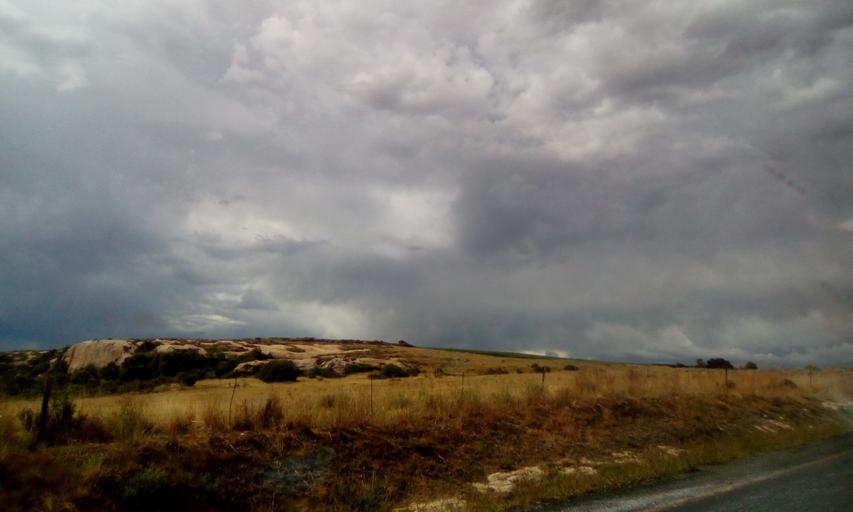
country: ZA
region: Orange Free State
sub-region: Thabo Mofutsanyana District Municipality
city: Ladybrand
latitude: -29.2462
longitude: 27.4455
